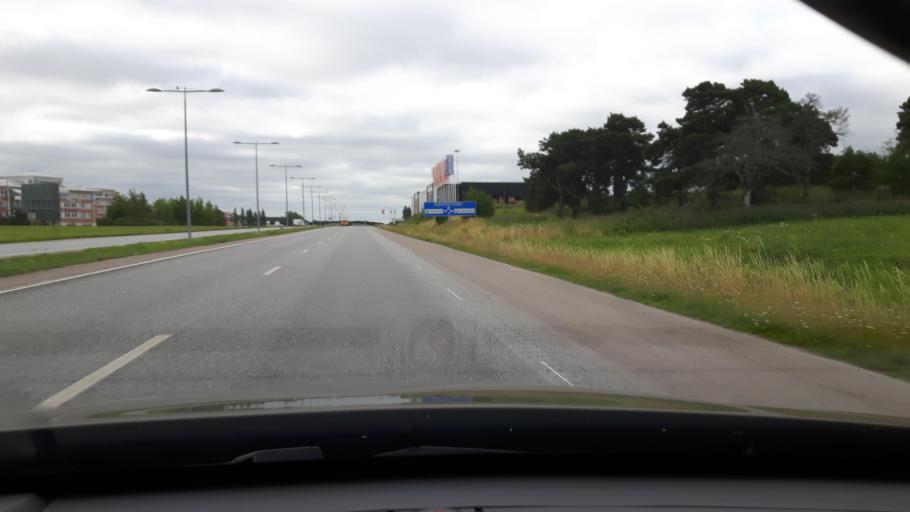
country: SE
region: Uppsala
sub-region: Uppsala Kommun
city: Uppsala
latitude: 59.8574
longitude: 17.6801
